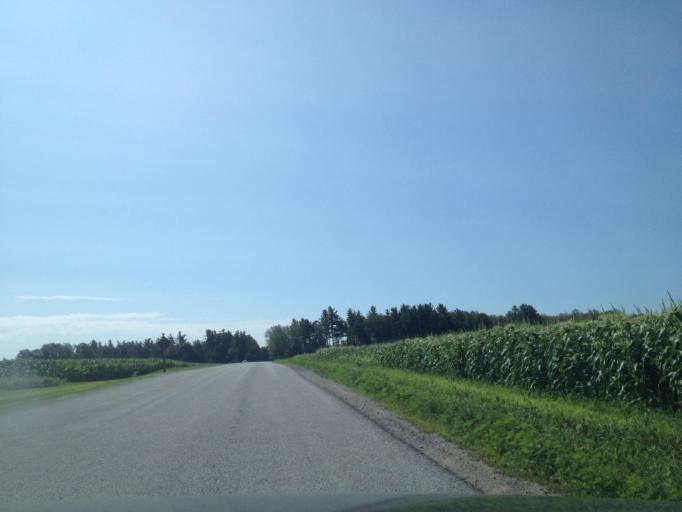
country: CA
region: Ontario
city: Norfolk County
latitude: 42.8304
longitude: -80.3885
